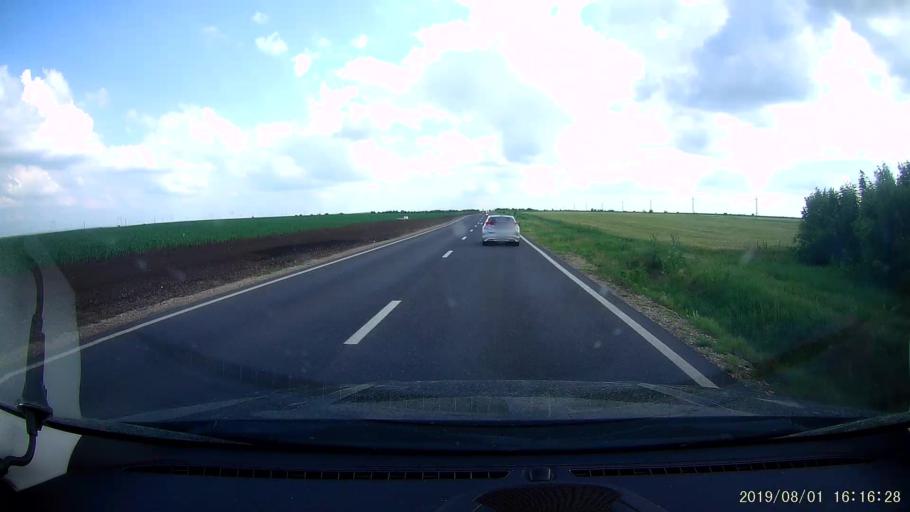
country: RO
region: Calarasi
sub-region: Comuna Stefan Voda
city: Stefan Voda
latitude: 44.3191
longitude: 27.3578
